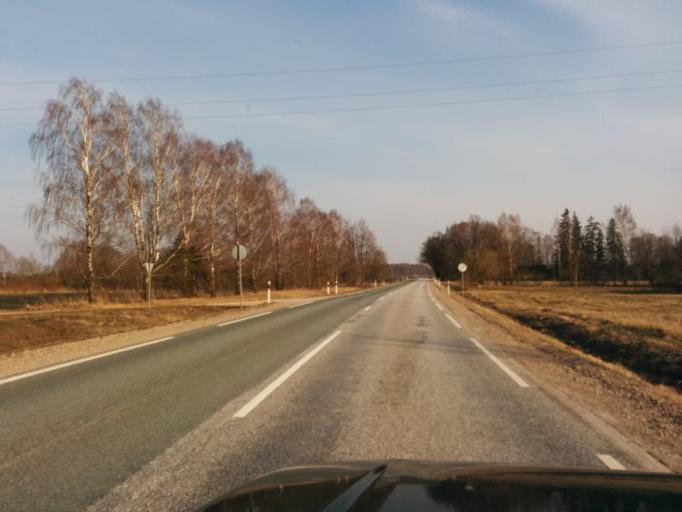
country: LV
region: Lecava
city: Iecava
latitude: 56.5934
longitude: 24.1296
